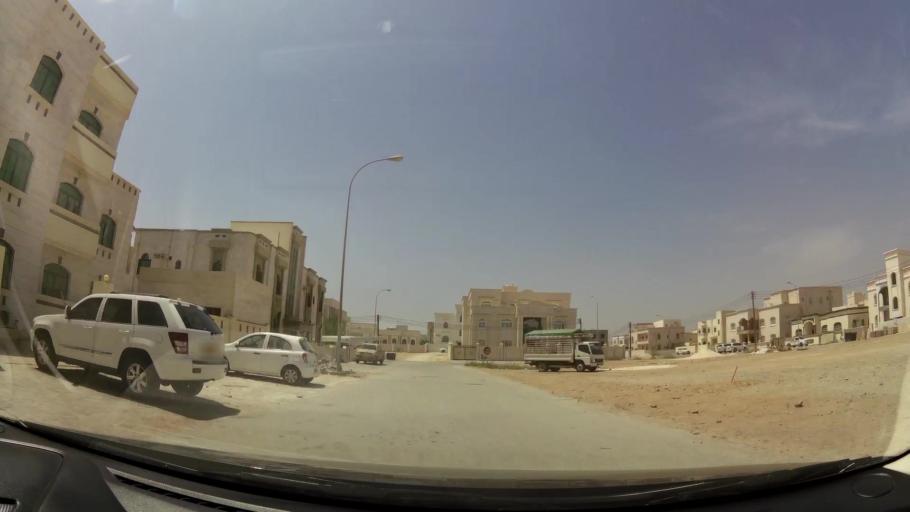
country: OM
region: Zufar
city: Salalah
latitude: 17.0544
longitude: 54.1609
